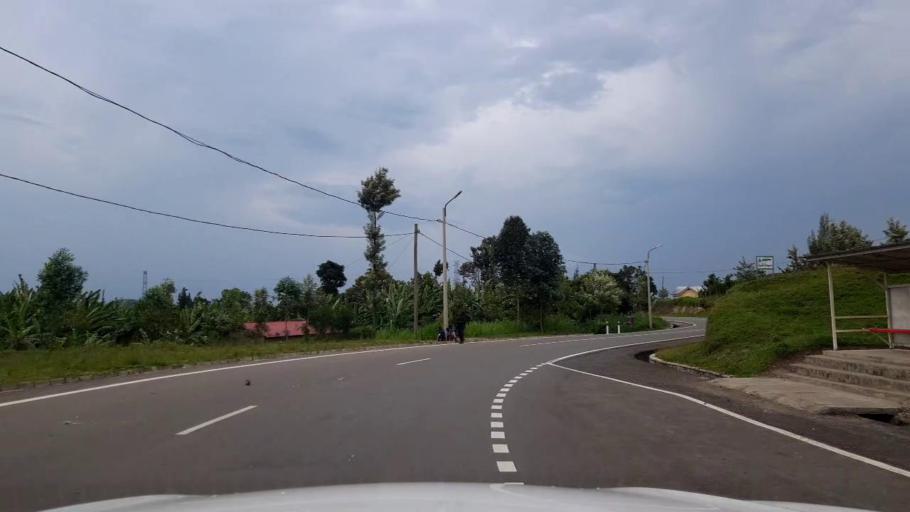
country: RW
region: Western Province
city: Kibuye
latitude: -2.0433
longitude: 29.4071
